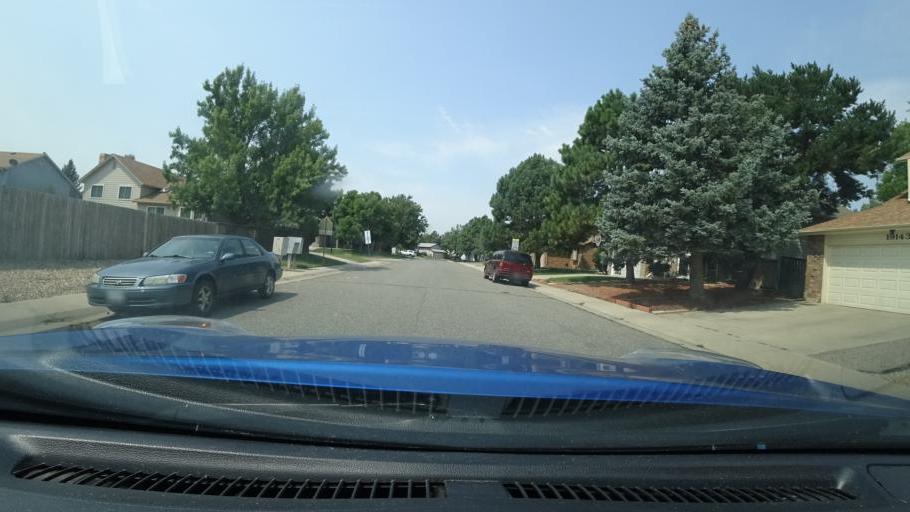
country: US
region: Colorado
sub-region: Adams County
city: Aurora
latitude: 39.7802
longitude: -104.7629
